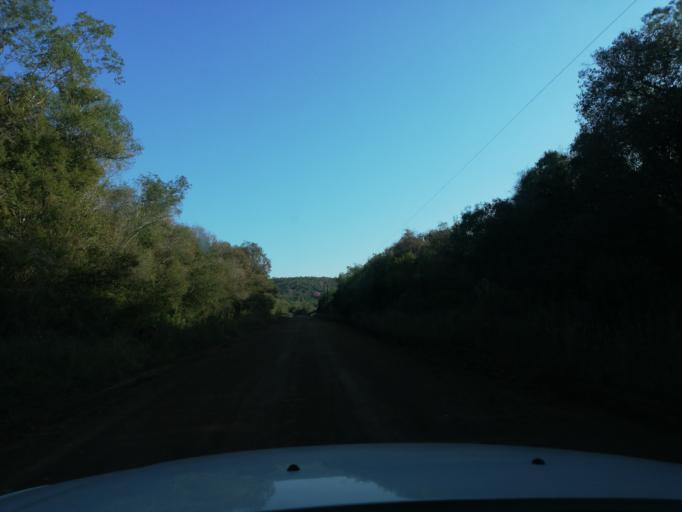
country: AR
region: Misiones
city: Cerro Cora
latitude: -27.6047
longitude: -55.7021
